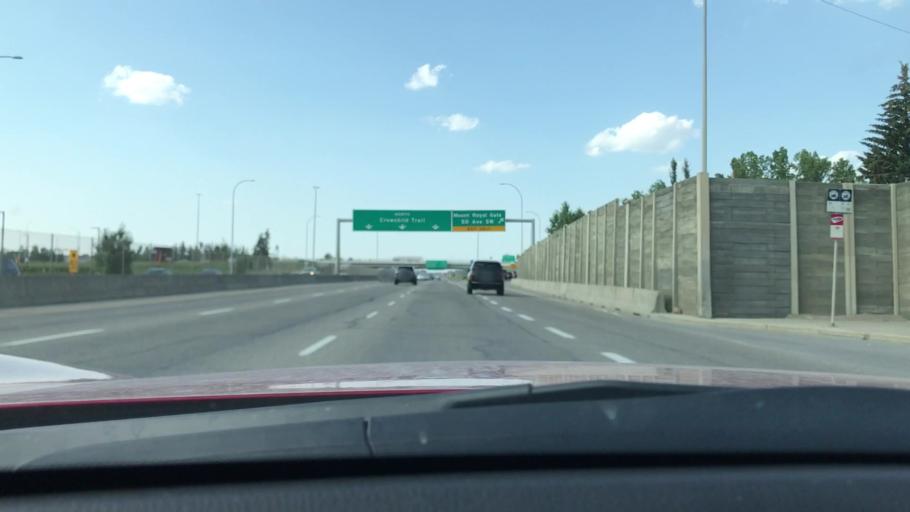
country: CA
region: Alberta
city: Calgary
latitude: 51.0057
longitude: -114.1179
